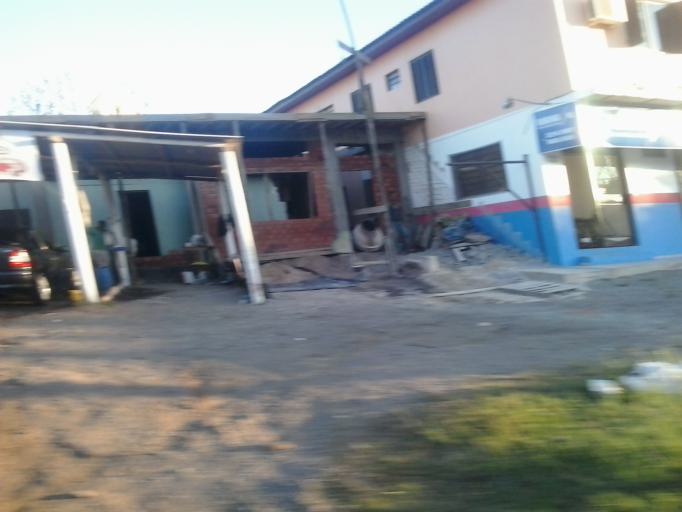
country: BR
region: Rio Grande do Sul
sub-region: Santa Maria
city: Santa Maria
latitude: -29.6971
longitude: -53.7349
